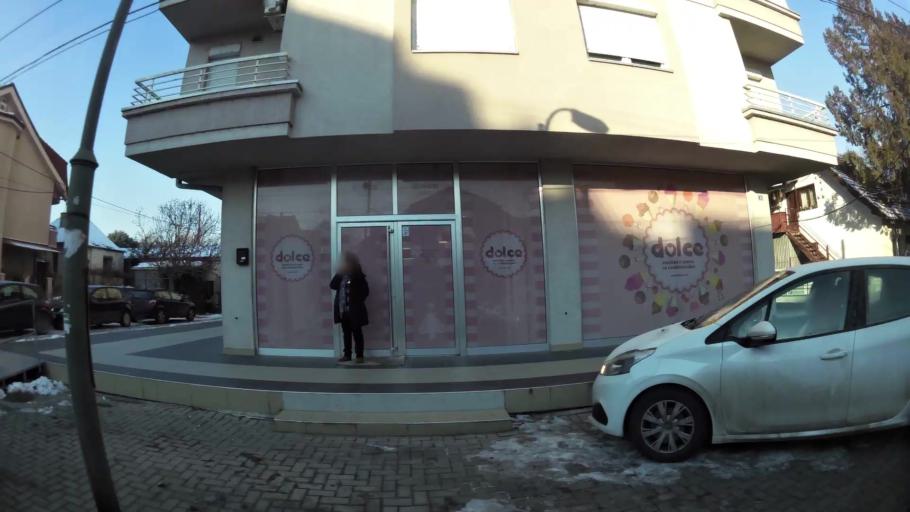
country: MK
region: Karpos
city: Skopje
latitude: 41.9972
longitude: 21.4148
